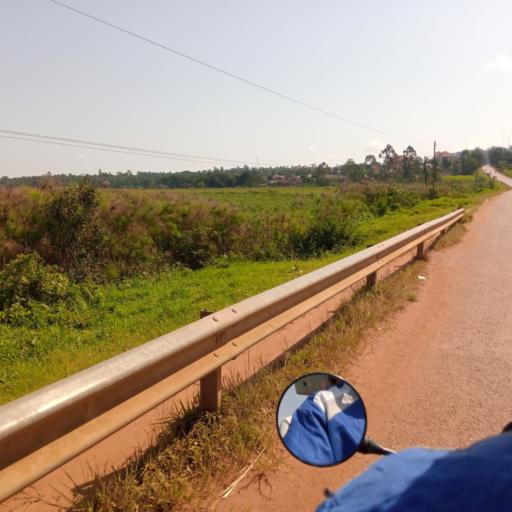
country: UG
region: Central Region
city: Masaka
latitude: -0.3532
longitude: 31.7230
